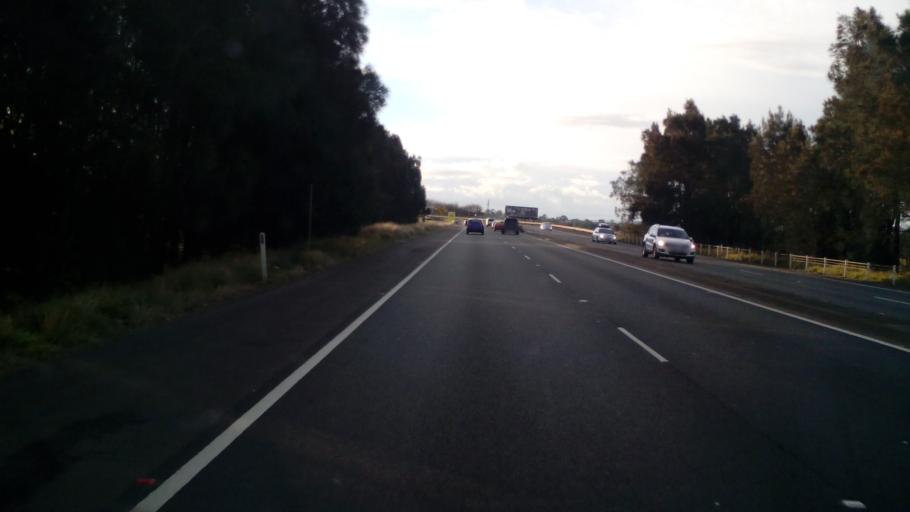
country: AU
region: New South Wales
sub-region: Newcastle
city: Beresfield
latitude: -32.8132
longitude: 151.6760
